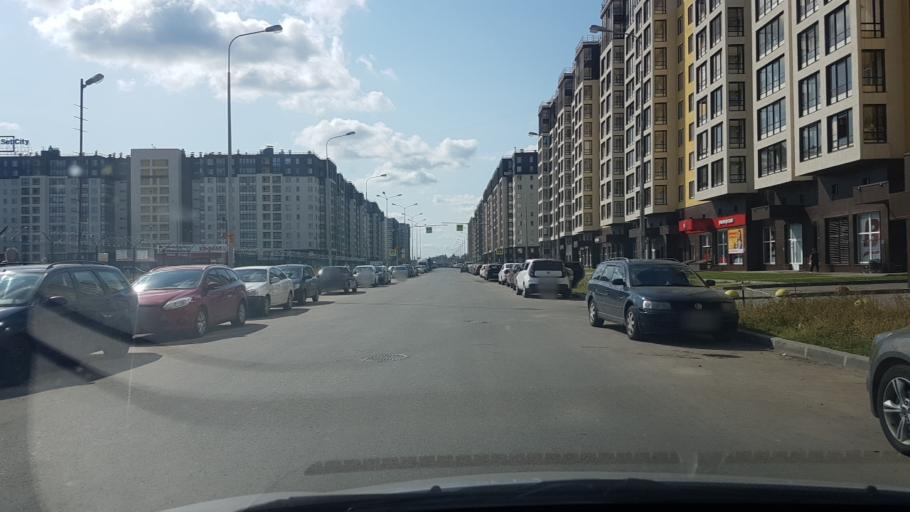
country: RU
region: St.-Petersburg
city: Sosnovaya Polyana
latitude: 59.8417
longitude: 30.1136
